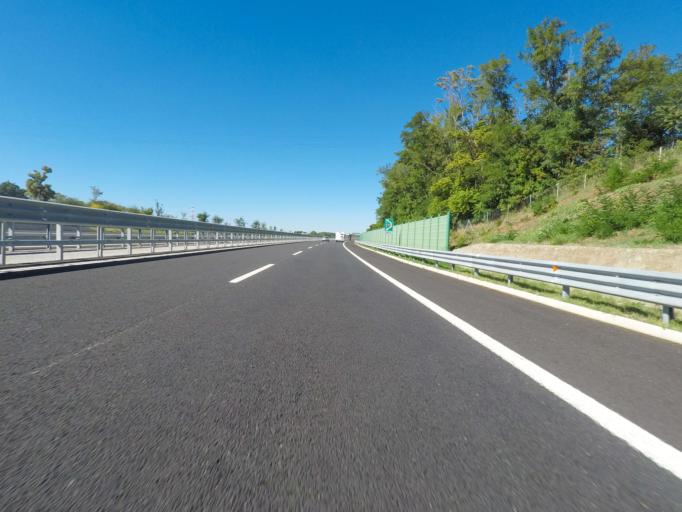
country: IT
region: Latium
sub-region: Provincia di Viterbo
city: Tarquinia
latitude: 42.2471
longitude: 11.7377
